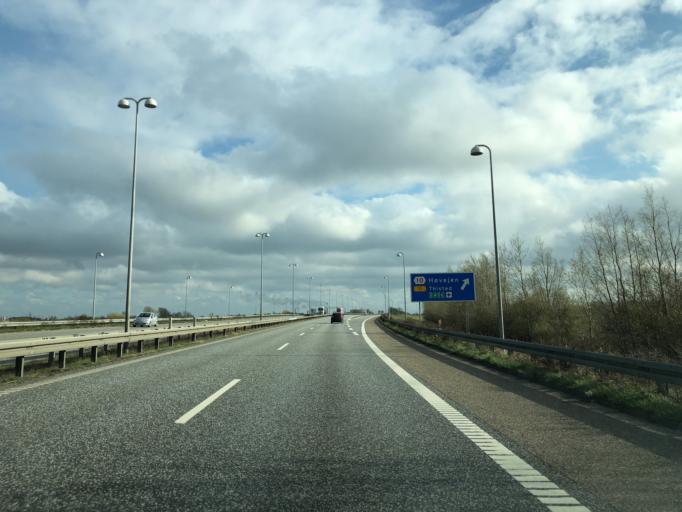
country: DK
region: North Denmark
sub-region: Alborg Kommune
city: Vestbjerg
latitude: 57.0956
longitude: 9.9672
